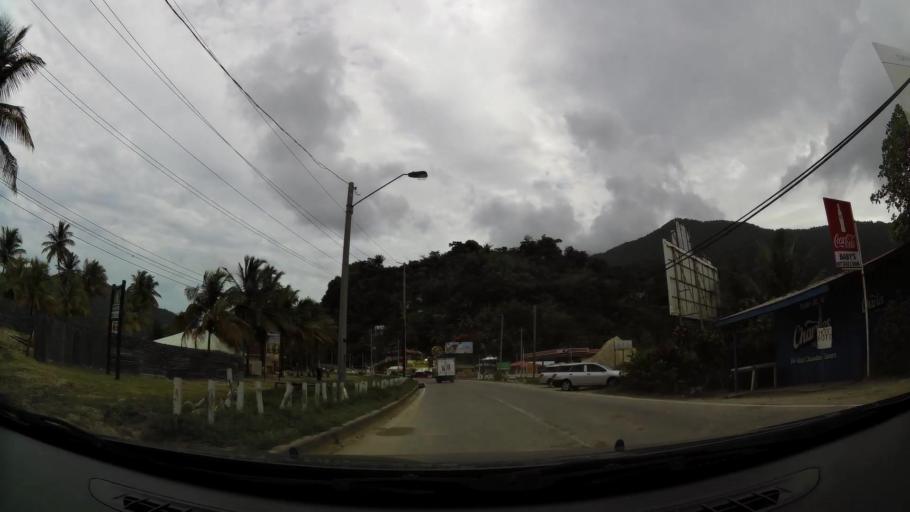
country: TT
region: Diego Martin
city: Petit Valley
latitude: 10.7577
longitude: -61.4379
